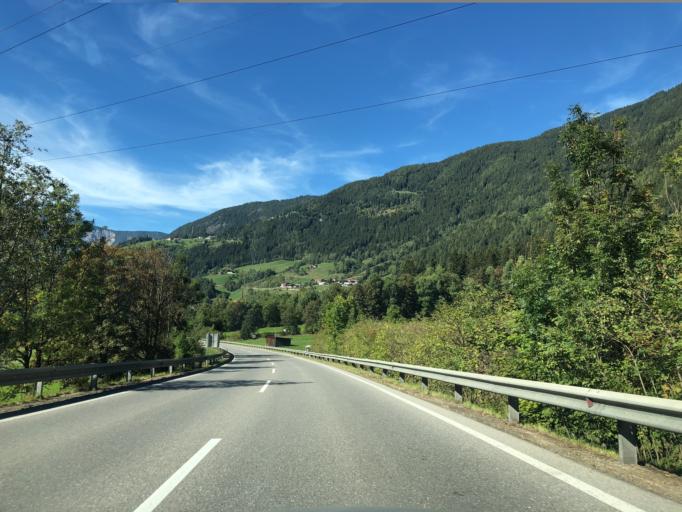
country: AT
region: Tyrol
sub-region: Politischer Bezirk Imst
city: Oetz
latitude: 47.1955
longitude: 10.9068
